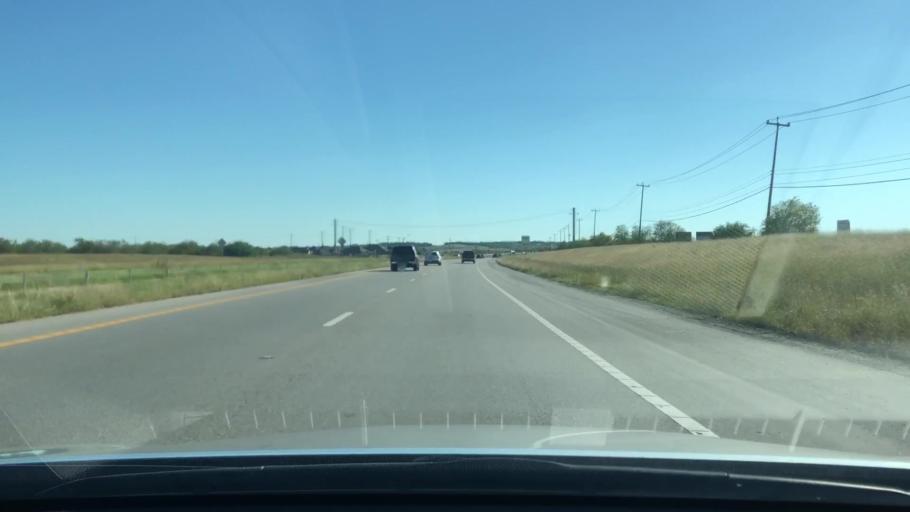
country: US
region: Texas
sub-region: Bexar County
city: Converse
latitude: 29.4948
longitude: -98.2898
